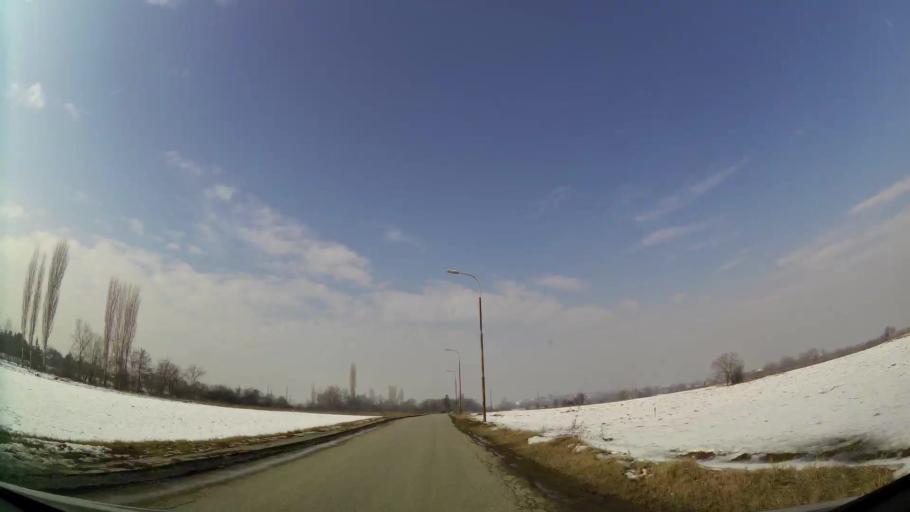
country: MK
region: Suto Orizari
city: Suto Orizare
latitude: 42.0174
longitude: 21.3896
